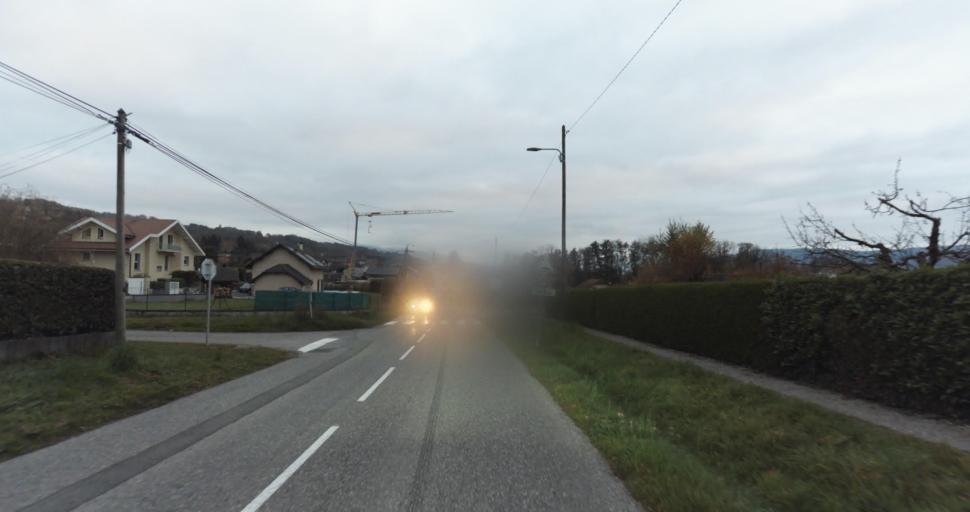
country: FR
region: Rhone-Alpes
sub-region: Departement de la Haute-Savoie
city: Saint-Felix
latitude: 45.8057
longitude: 5.9724
